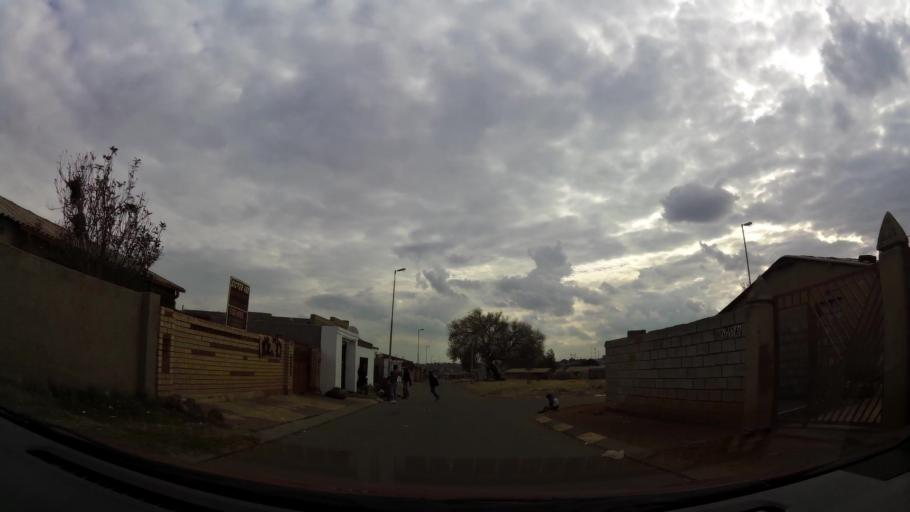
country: ZA
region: Gauteng
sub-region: City of Johannesburg Metropolitan Municipality
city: Soweto
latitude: -26.2476
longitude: 27.8449
